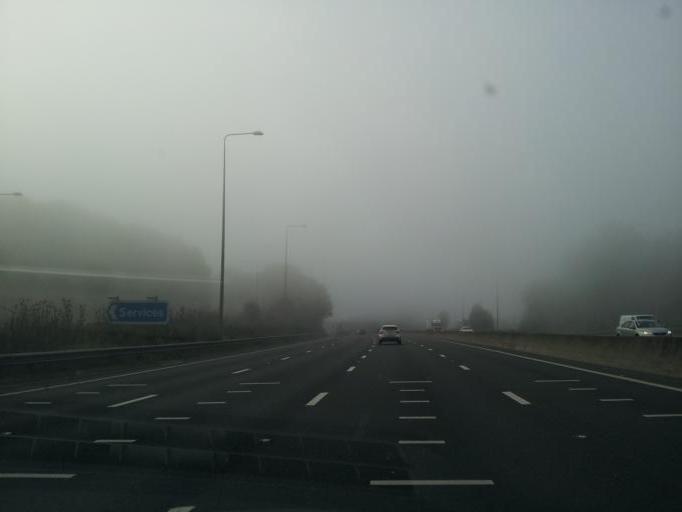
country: GB
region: England
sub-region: Kirklees
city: Cleckheaton
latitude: 53.7165
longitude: -1.7453
